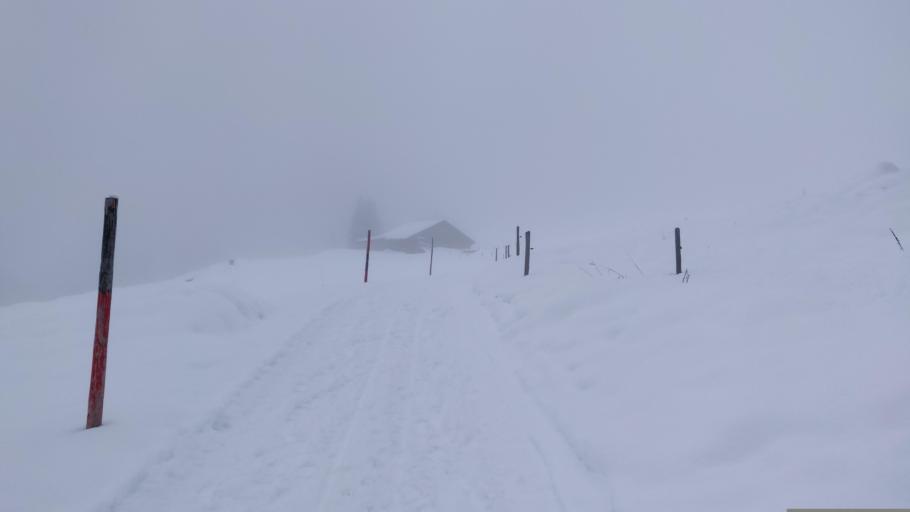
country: CH
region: Bern
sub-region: Interlaken-Oberhasli District
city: Lauterbrunnen
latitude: 46.5895
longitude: 7.8927
